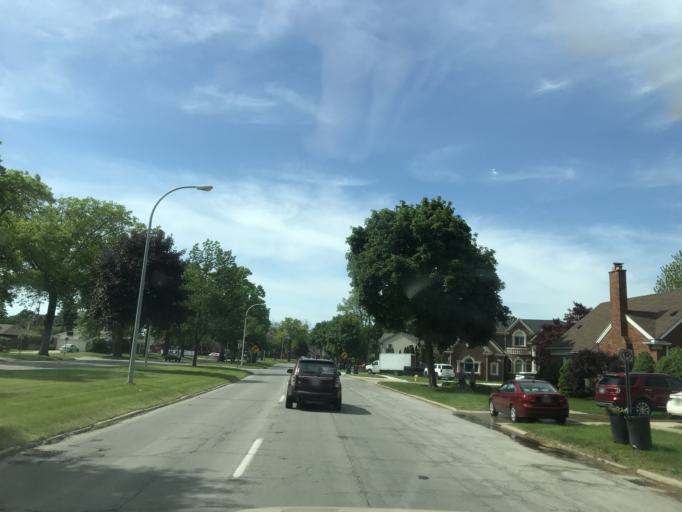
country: US
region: Michigan
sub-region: Wayne County
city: Dearborn Heights
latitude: 42.3236
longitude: -83.2600
